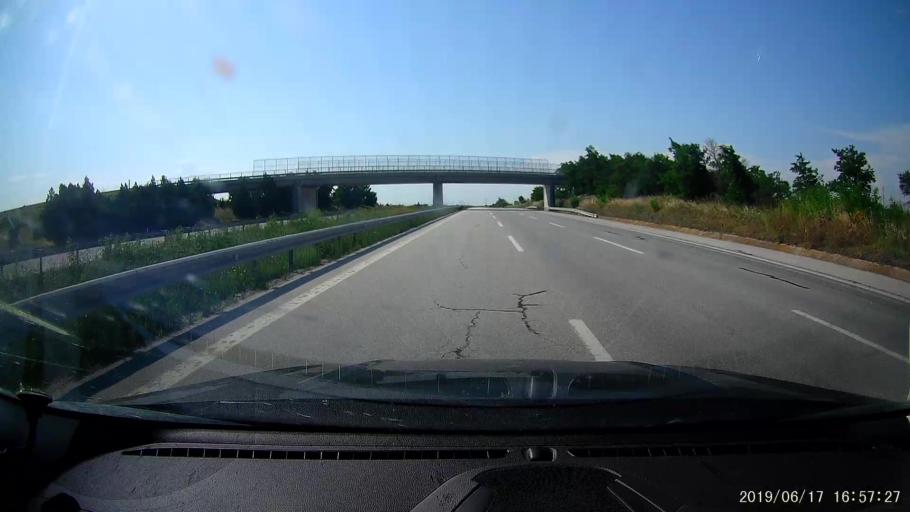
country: TR
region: Edirne
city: Haskoy
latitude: 41.6008
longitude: 26.9143
